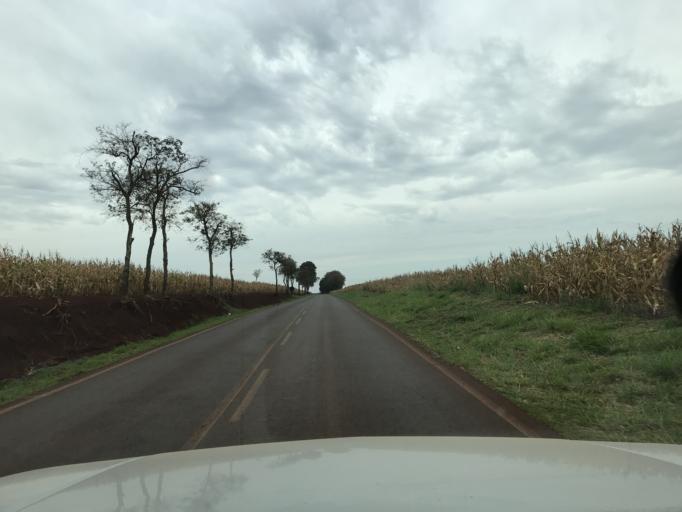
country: BR
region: Parana
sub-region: Palotina
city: Palotina
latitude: -24.4341
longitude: -53.9123
